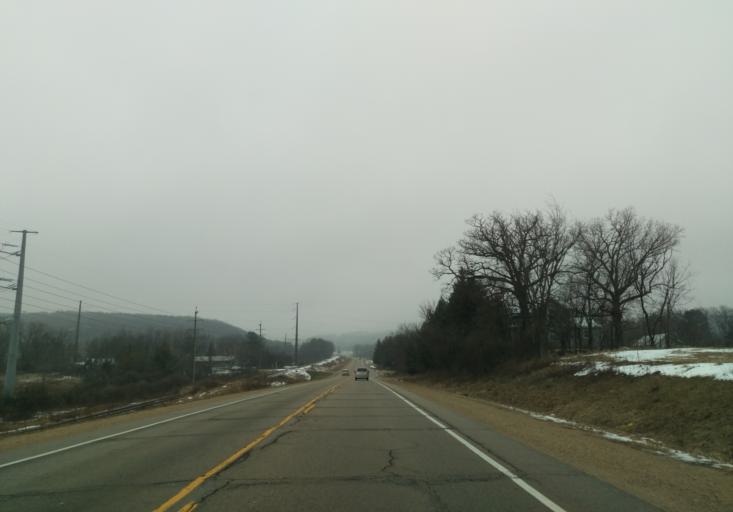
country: US
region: Wisconsin
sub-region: Dane County
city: Middleton
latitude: 43.0954
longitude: -89.5631
